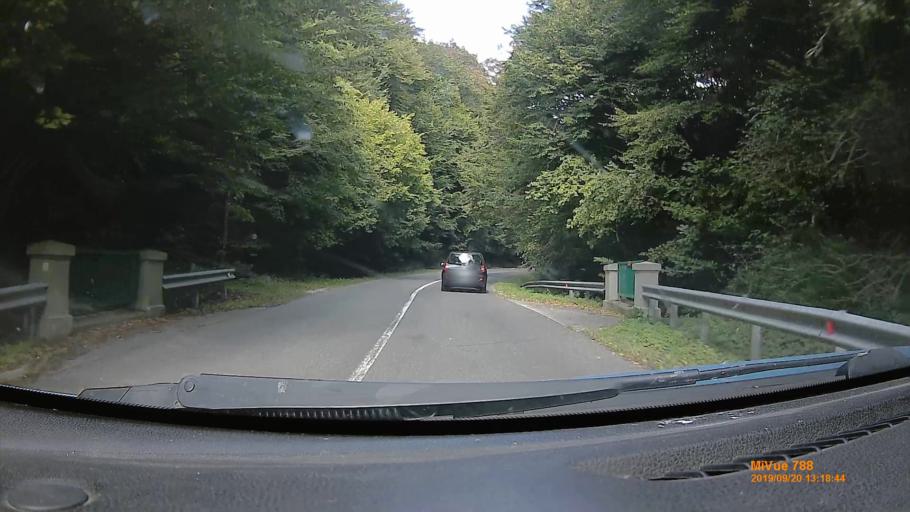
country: HU
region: Heves
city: Felsotarkany
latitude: 48.0026
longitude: 20.4643
